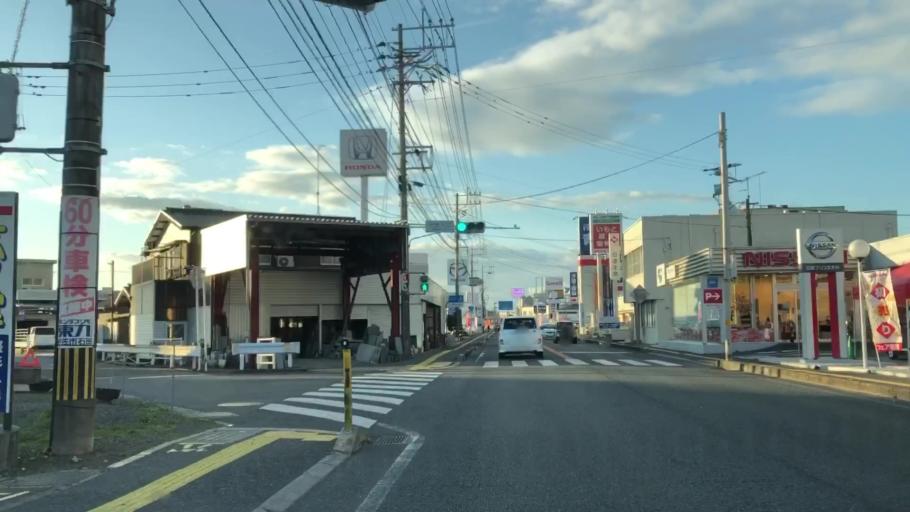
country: JP
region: Oita
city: Bungo-Takada-shi
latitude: 33.5330
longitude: 131.3314
